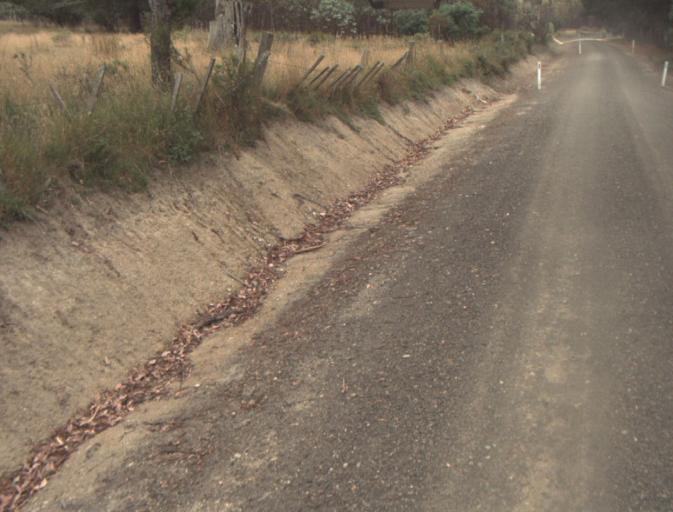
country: AU
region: Tasmania
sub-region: Northern Midlands
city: Evandale
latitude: -41.4567
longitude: 147.4454
